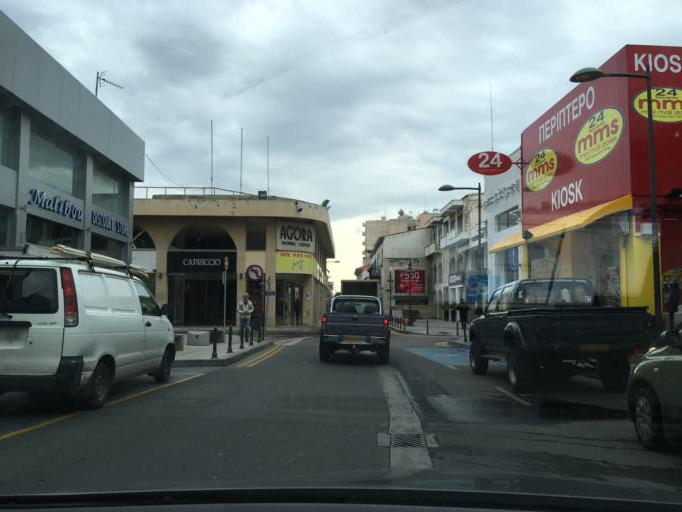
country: CY
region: Limassol
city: Limassol
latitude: 34.6763
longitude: 33.0454
